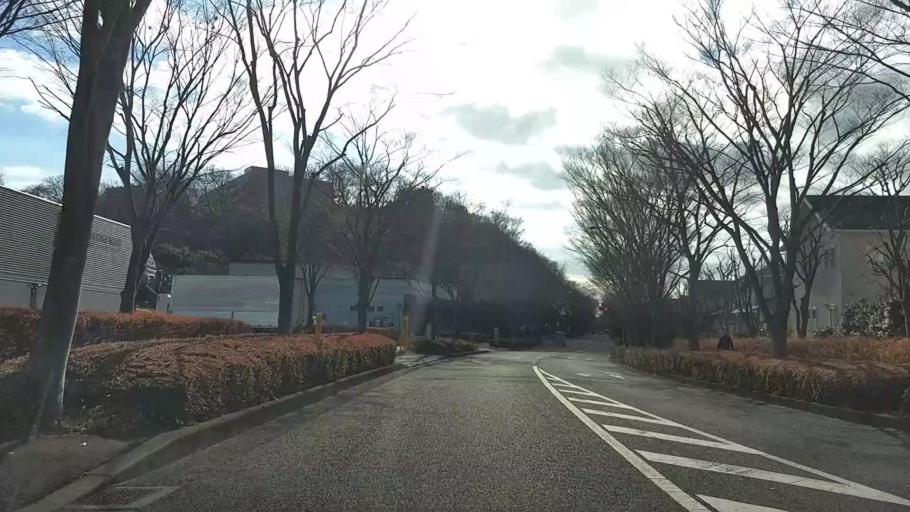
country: JP
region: Kanagawa
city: Atsugi
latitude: 35.4489
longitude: 139.3107
